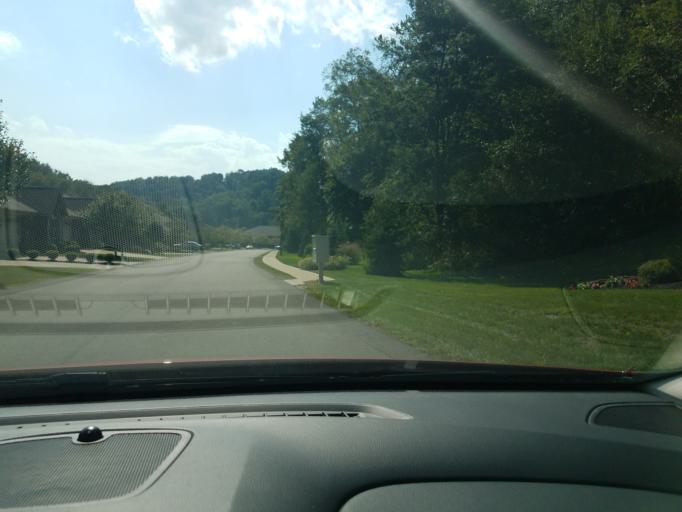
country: US
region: Pennsylvania
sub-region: Allegheny County
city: Franklin Park
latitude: 40.5594
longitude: -80.0545
